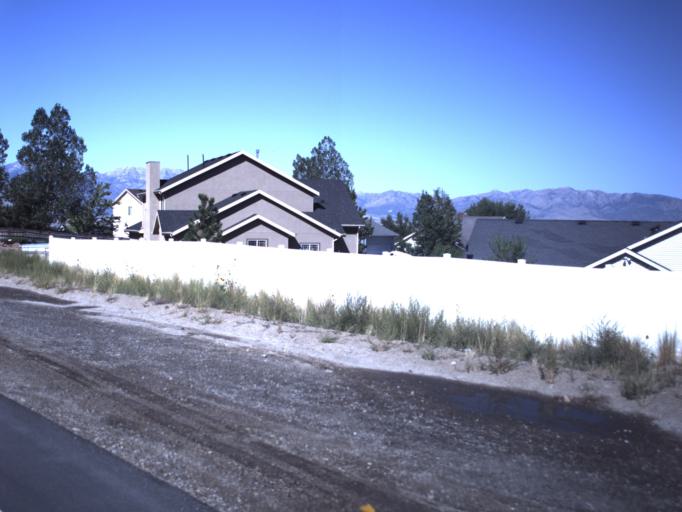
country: US
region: Utah
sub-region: Tooele County
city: Tooele
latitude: 40.5161
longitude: -112.3054
